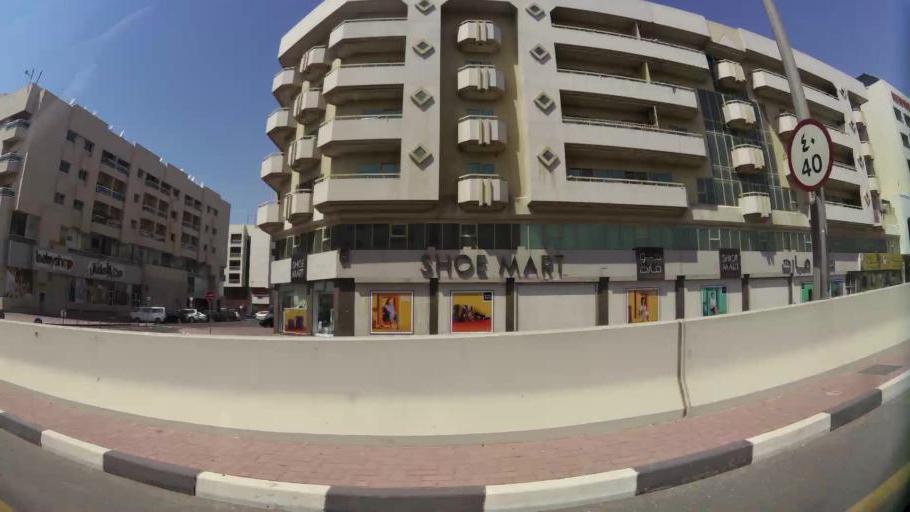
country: AE
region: Ash Shariqah
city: Sharjah
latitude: 25.2773
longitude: 55.3468
